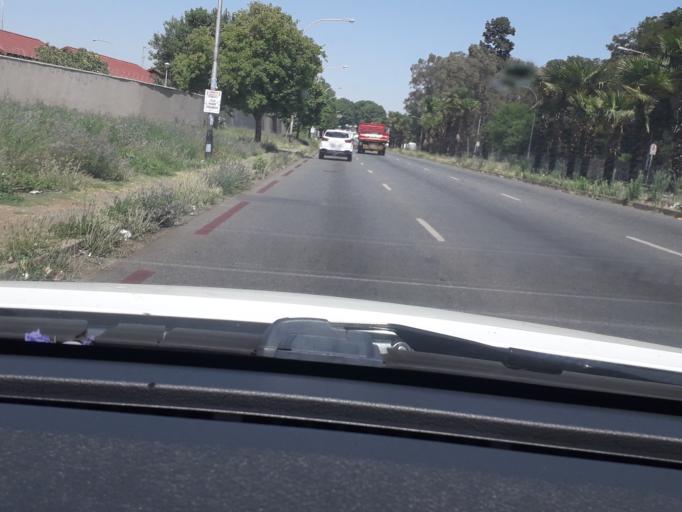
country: ZA
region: Gauteng
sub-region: City of Johannesburg Metropolitan Municipality
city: Johannesburg
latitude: -26.1855
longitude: 28.1013
